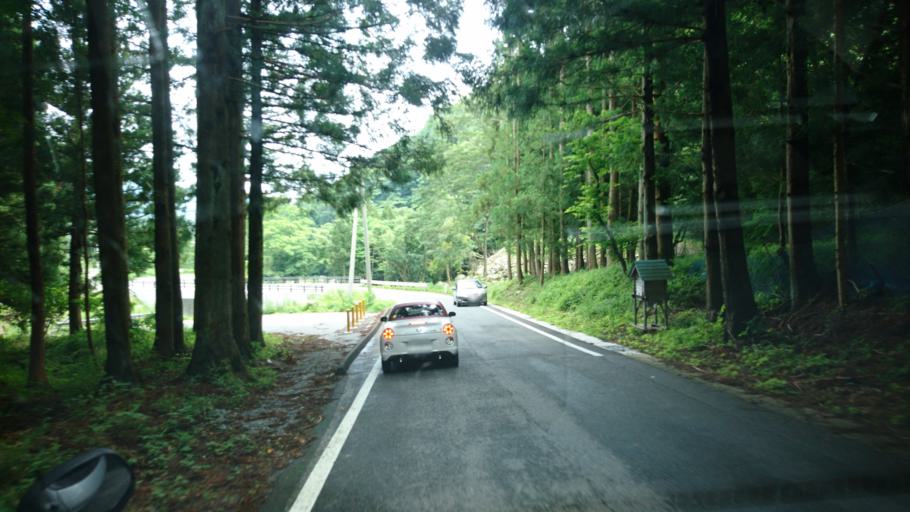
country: JP
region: Iwate
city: Ofunato
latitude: 39.1320
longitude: 141.7936
